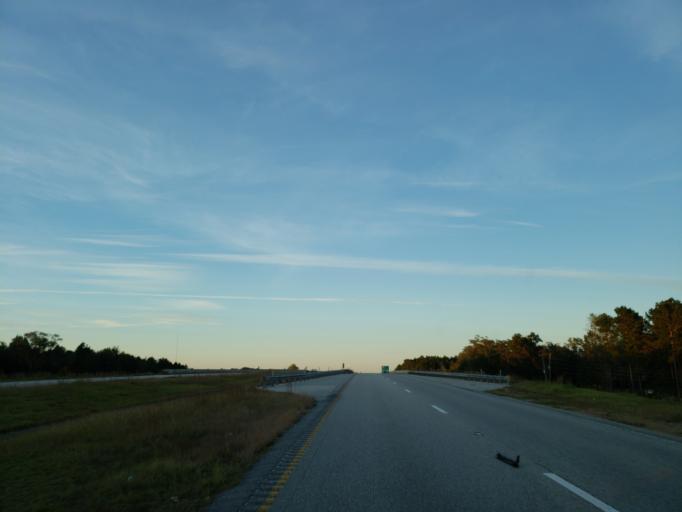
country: US
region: Mississippi
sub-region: Wayne County
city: Belmont
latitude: 31.4442
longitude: -88.4652
